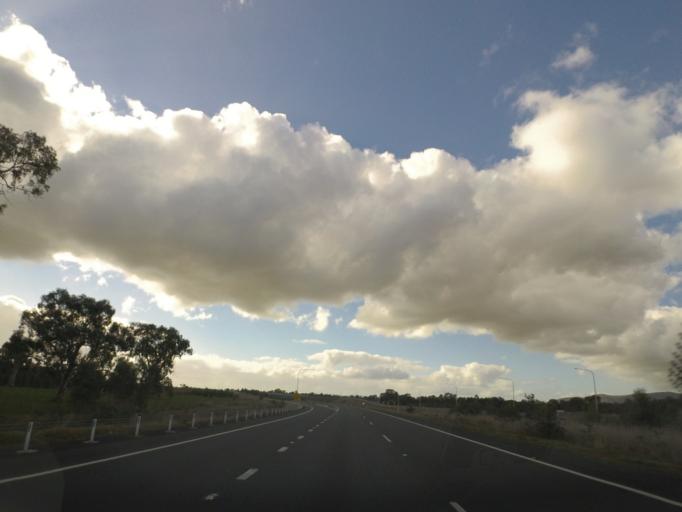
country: AU
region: New South Wales
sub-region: Greater Hume Shire
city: Holbrook
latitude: -35.7380
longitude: 147.3042
